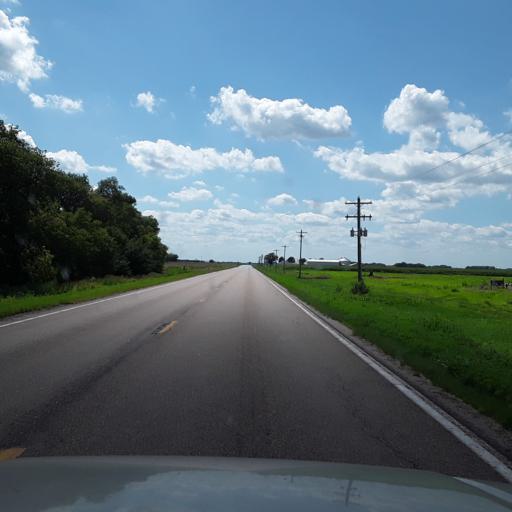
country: US
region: Nebraska
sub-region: Merrick County
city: Central City
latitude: 41.1910
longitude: -98.0280
